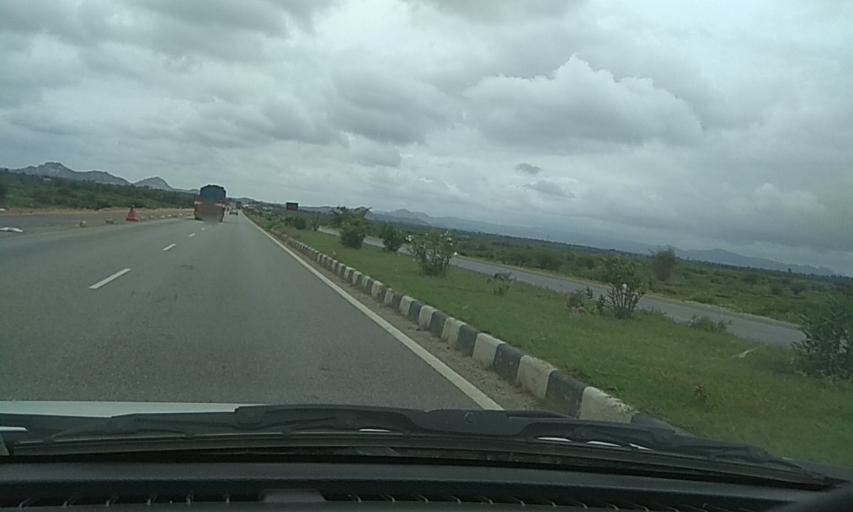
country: IN
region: Karnataka
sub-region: Chitradurga
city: Chitradurga
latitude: 14.2789
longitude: 76.3109
